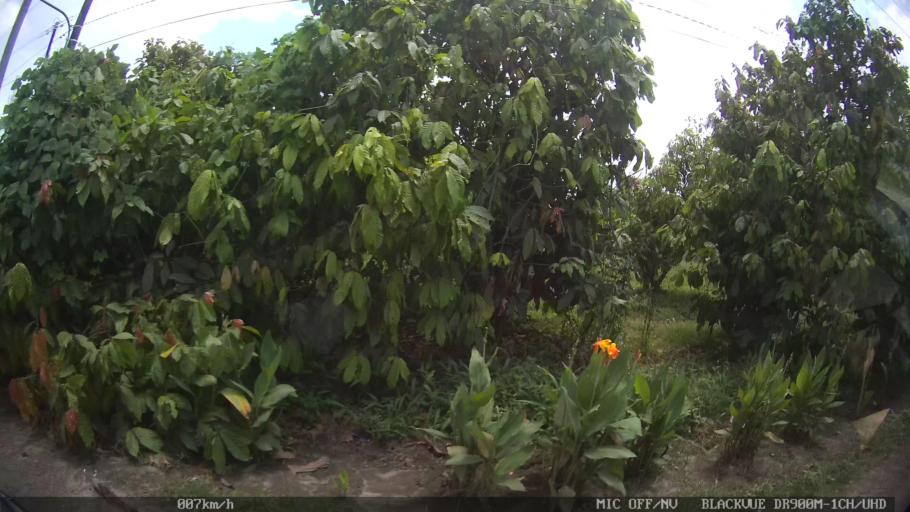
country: ID
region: North Sumatra
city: Perbaungan
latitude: 3.5274
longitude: 98.8882
